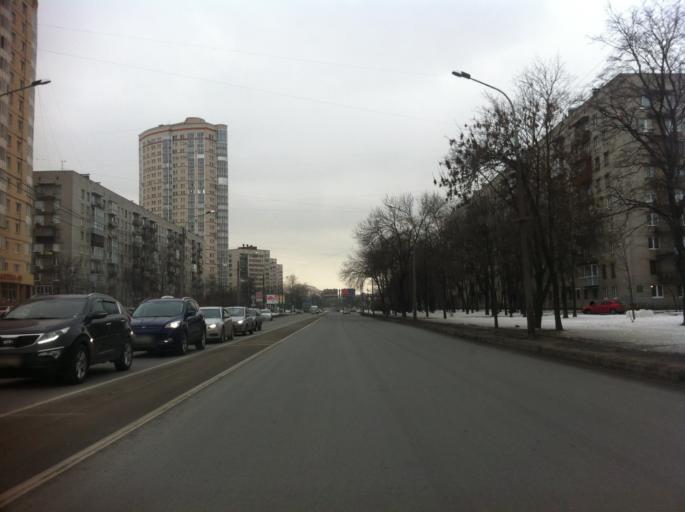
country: RU
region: St.-Petersburg
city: Dachnoye
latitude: 59.8425
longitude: 30.2538
